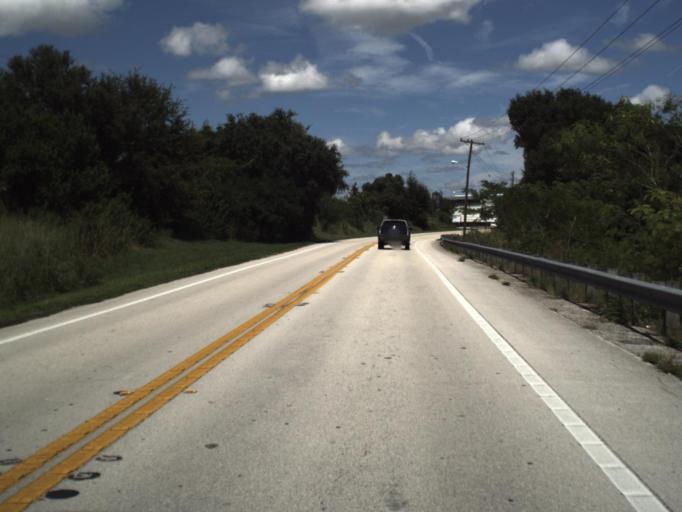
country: US
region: Florida
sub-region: Polk County
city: Lake Hamilton
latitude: 28.0446
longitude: -81.6207
